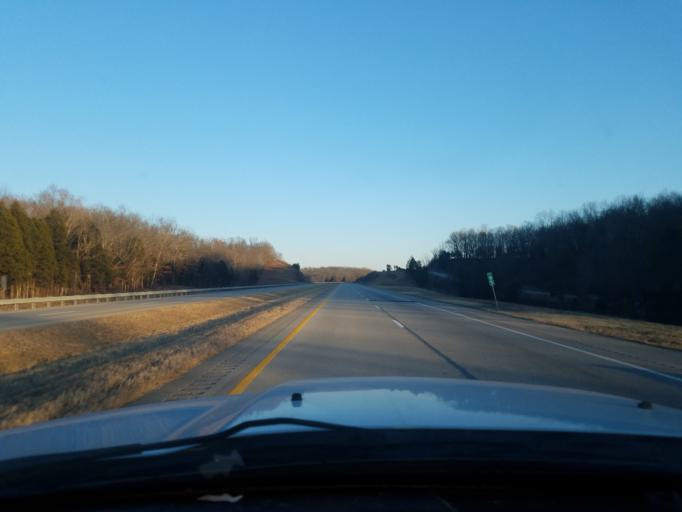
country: US
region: Kentucky
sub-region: Ohio County
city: Oak Grove
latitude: 37.3858
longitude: -86.6637
